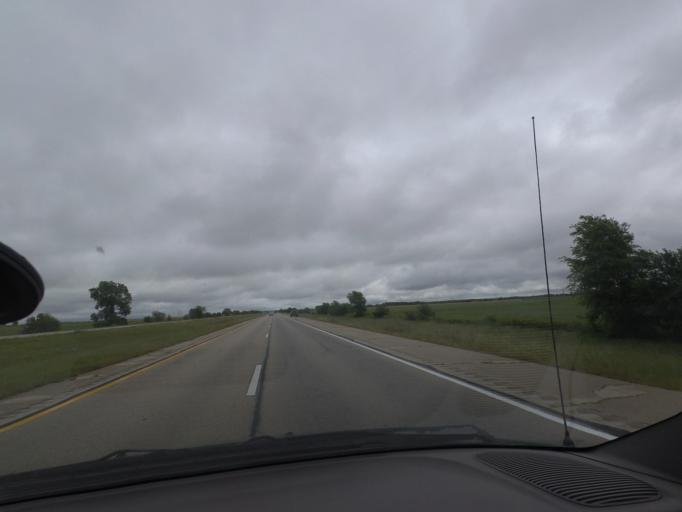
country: US
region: Illinois
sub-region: Piatt County
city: Monticello
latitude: 40.0211
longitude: -88.7035
